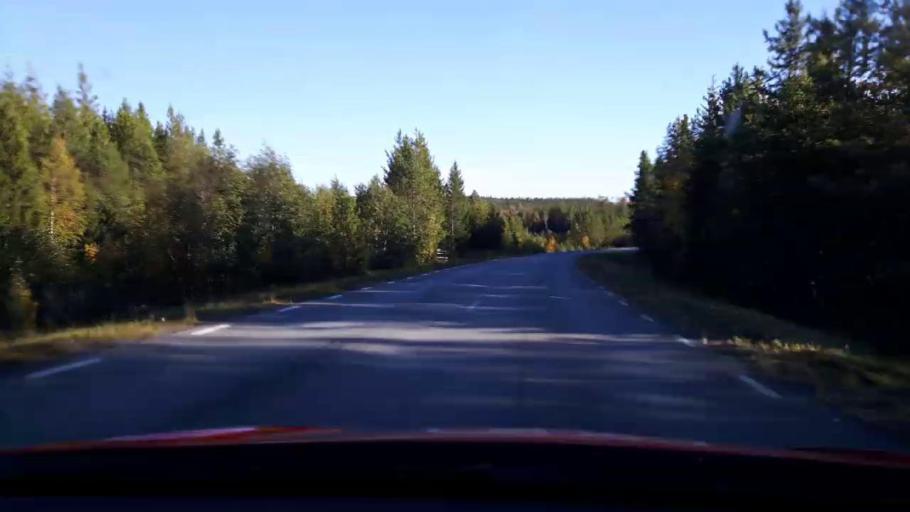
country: SE
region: Jaemtland
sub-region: OEstersunds Kommun
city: Lit
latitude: 63.7682
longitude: 14.7213
